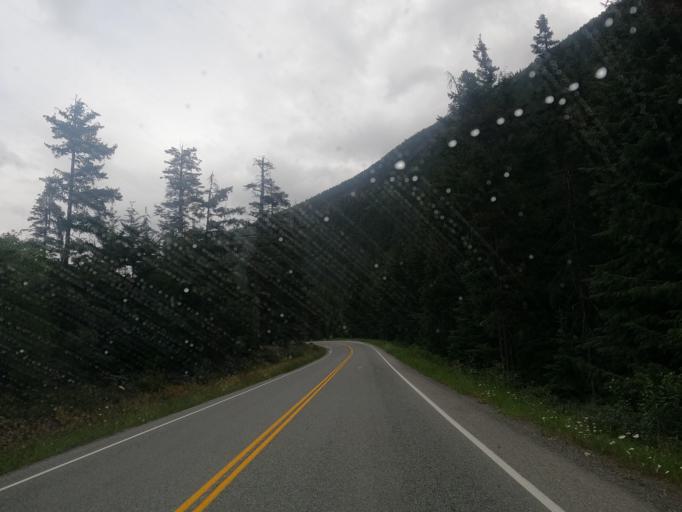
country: CA
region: British Columbia
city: Lillooet
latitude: 50.5058
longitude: -122.1759
